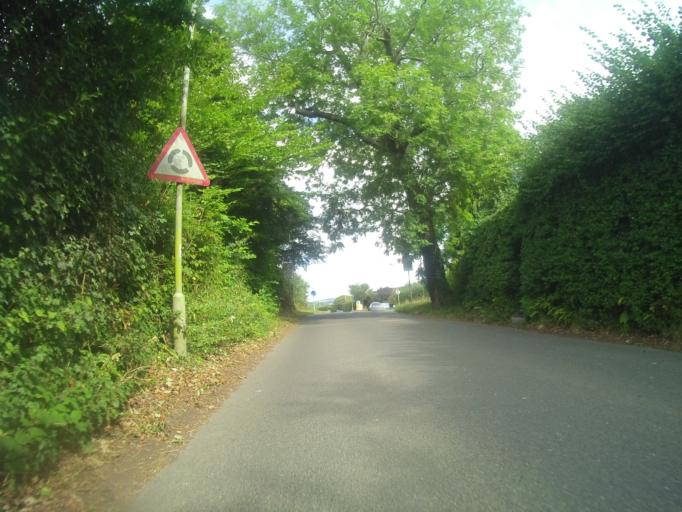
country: GB
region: England
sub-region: Devon
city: Totnes
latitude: 50.4403
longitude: -3.7059
